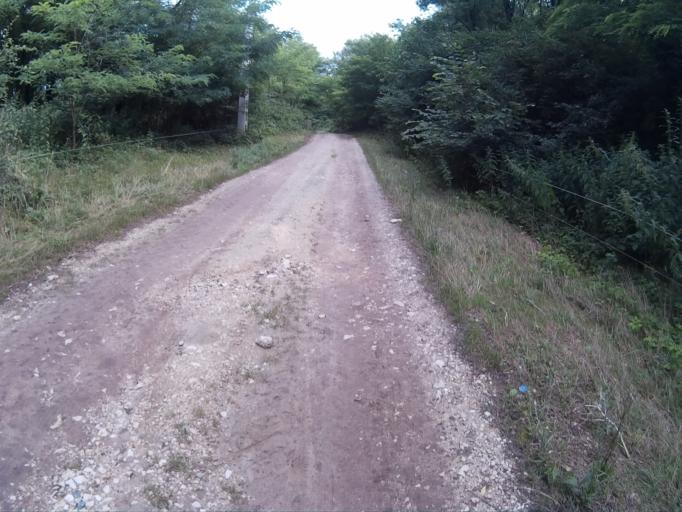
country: HU
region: Veszprem
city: Papa
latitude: 47.2847
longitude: 17.5772
